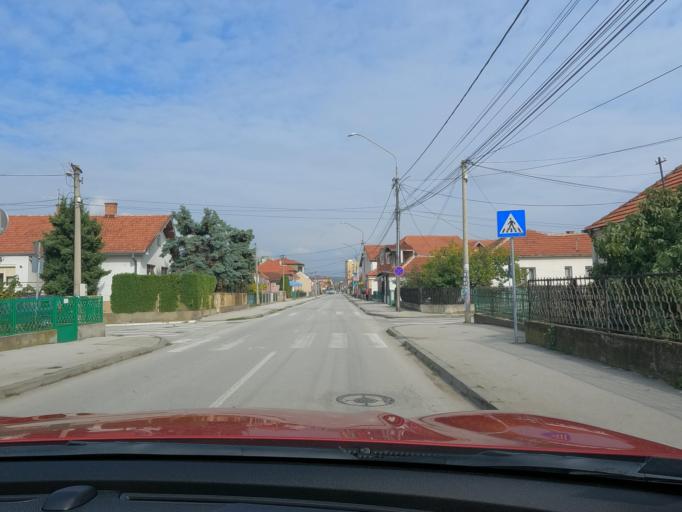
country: RS
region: Central Serbia
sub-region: Moravicki Okrug
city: Cacak
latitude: 43.8822
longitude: 20.3402
